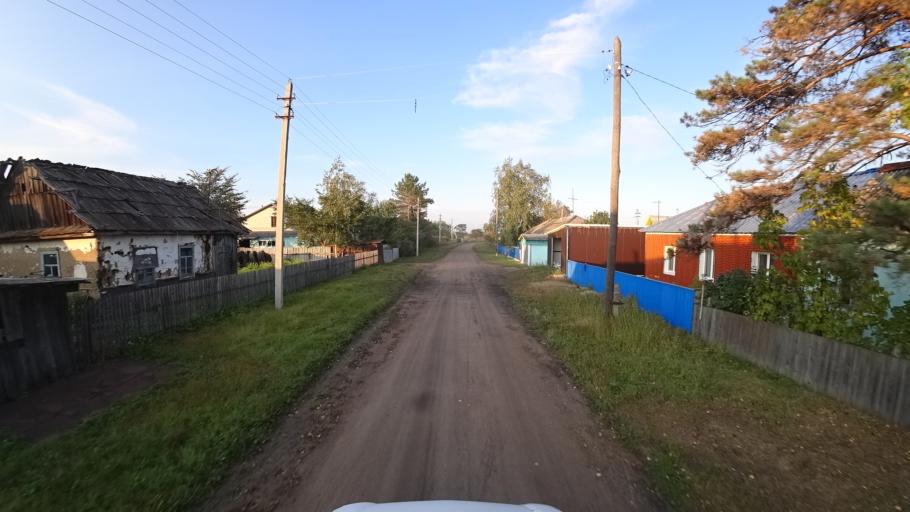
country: RU
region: Amur
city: Arkhara
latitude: 49.3646
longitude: 130.1139
